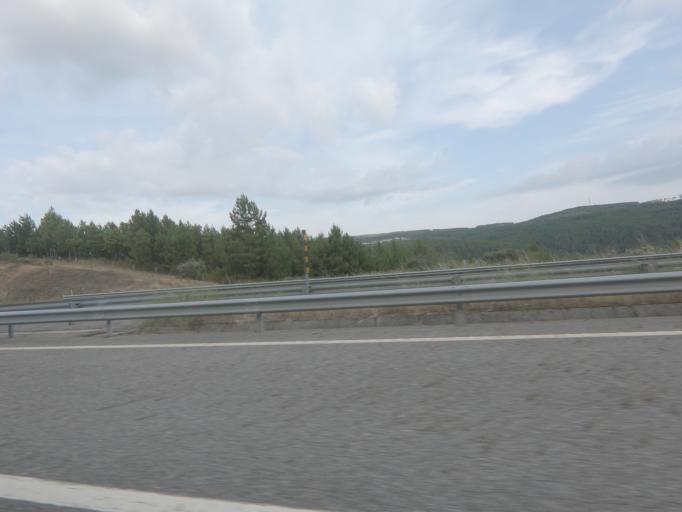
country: PT
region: Vila Real
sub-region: Chaves
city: Chaves
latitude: 41.6913
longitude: -7.5587
